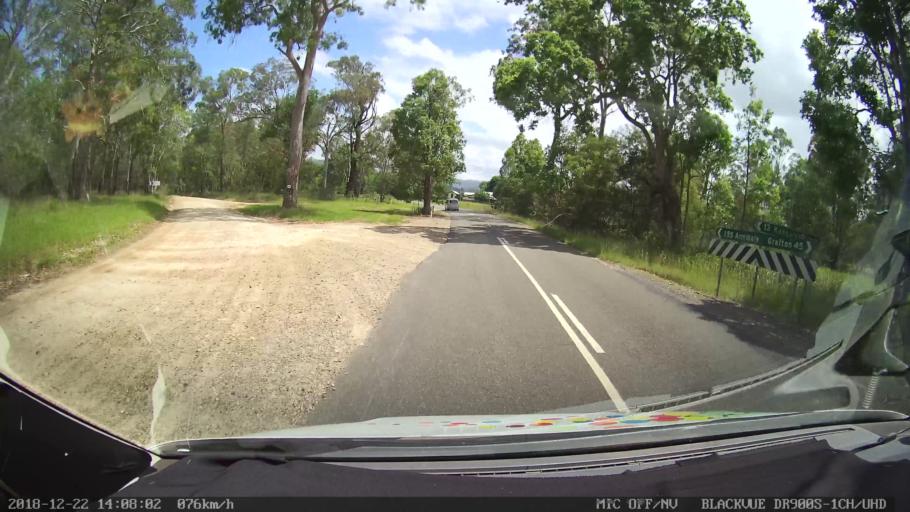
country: AU
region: New South Wales
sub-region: Clarence Valley
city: Coutts Crossing
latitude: -29.9741
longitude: 152.7259
